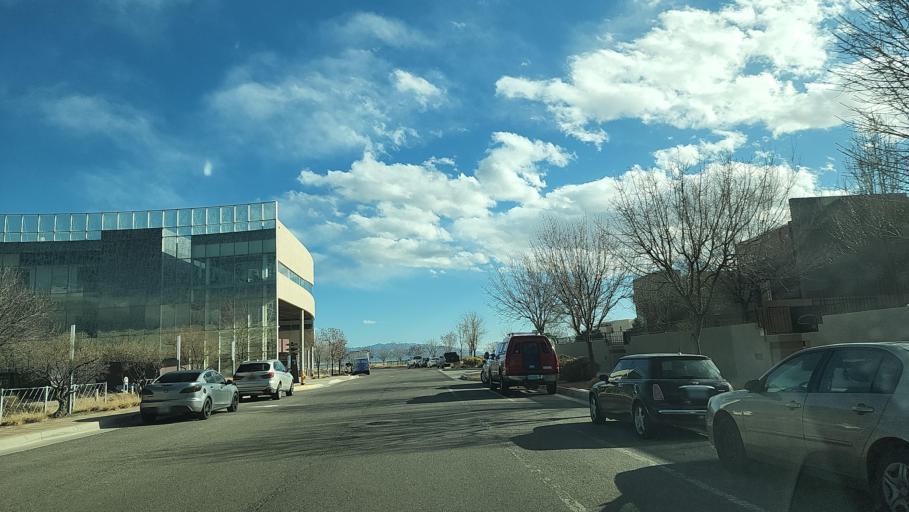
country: US
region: New Mexico
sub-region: Bernalillo County
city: South Valley
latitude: 34.9872
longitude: -106.6143
